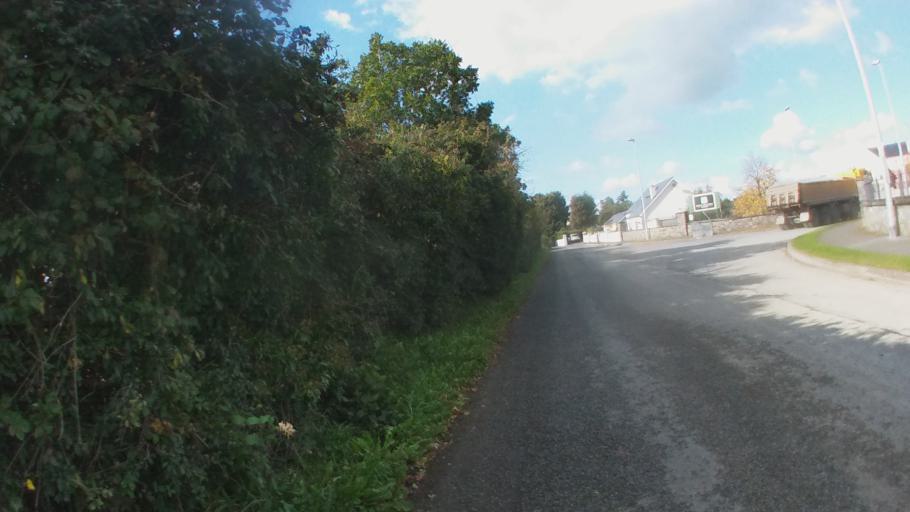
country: IE
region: Leinster
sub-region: Kilkenny
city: Kilkenny
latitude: 52.6698
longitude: -7.2330
